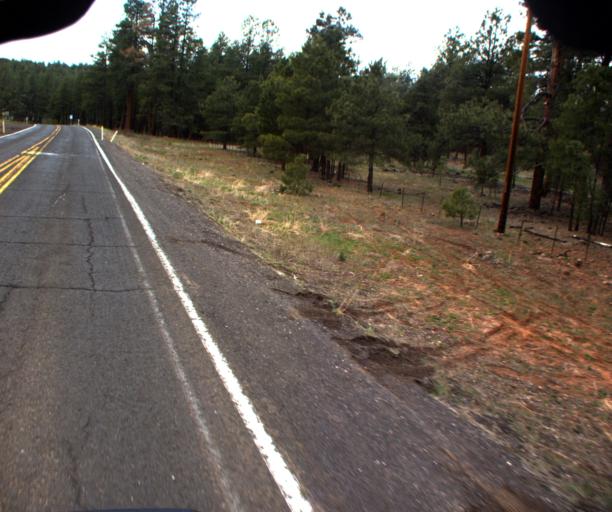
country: US
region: Arizona
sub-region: Coconino County
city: Kachina Village
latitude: 35.1214
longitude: -111.7045
